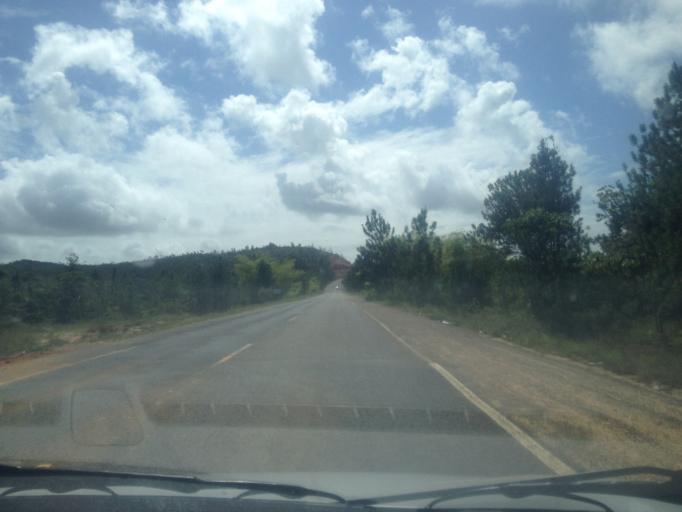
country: BR
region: Bahia
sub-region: Conde
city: Conde
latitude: -11.9884
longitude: -37.6780
